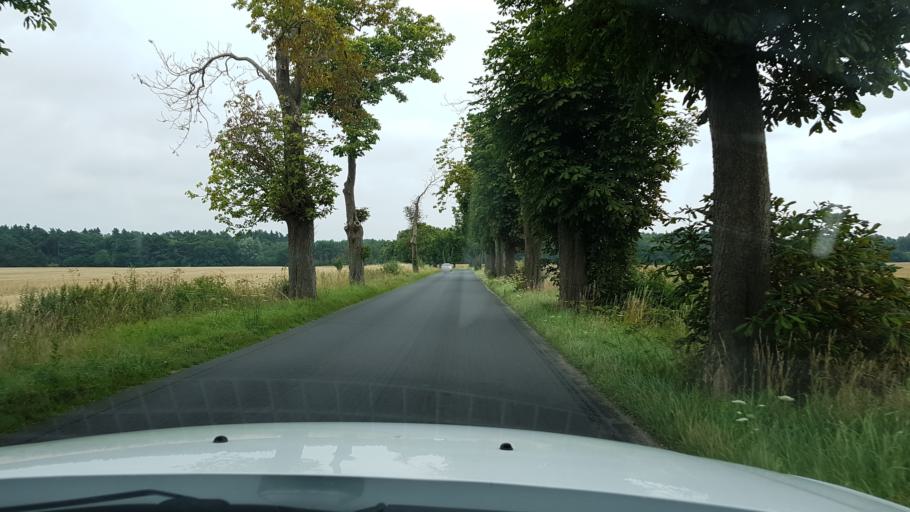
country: PL
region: West Pomeranian Voivodeship
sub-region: Powiat slawienski
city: Slawno
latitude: 54.5006
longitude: 16.5747
